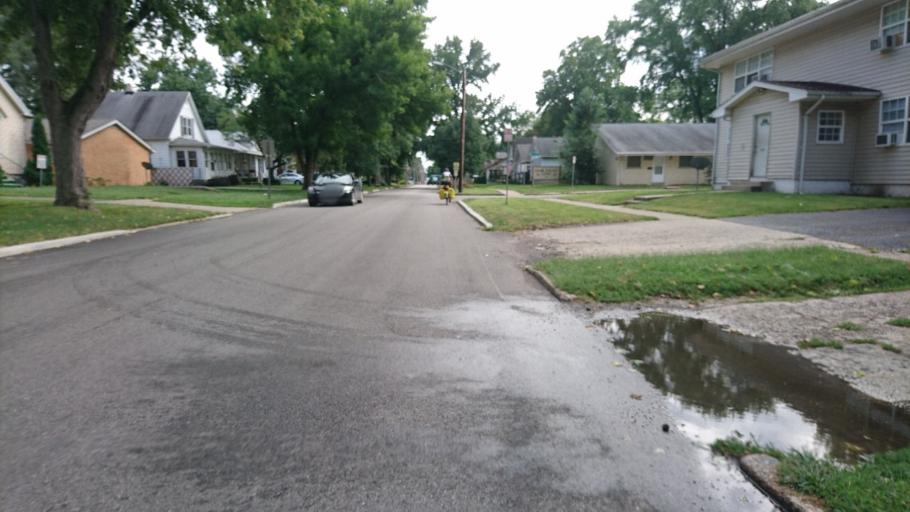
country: US
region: Illinois
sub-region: Sangamon County
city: Springfield
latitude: 39.7810
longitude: -89.6544
